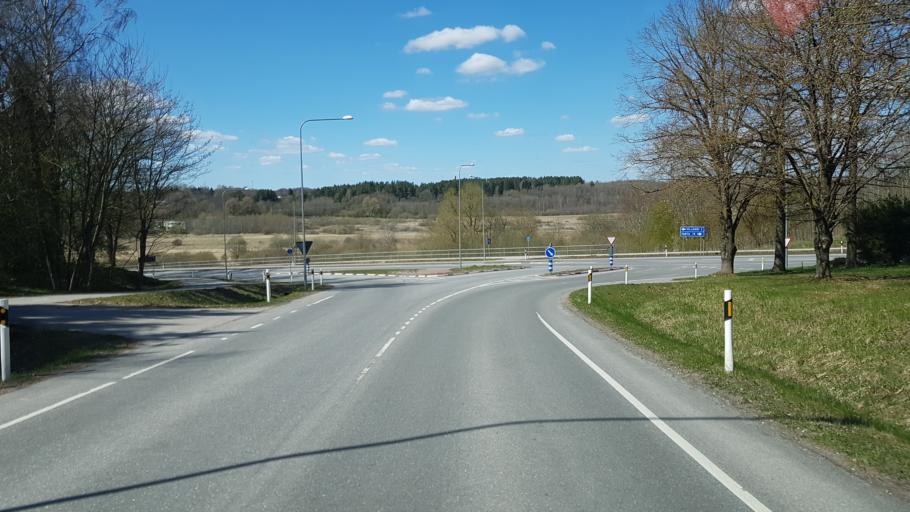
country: EE
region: Viljandimaa
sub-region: Viiratsi vald
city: Viiratsi
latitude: 58.3628
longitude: 25.6395
